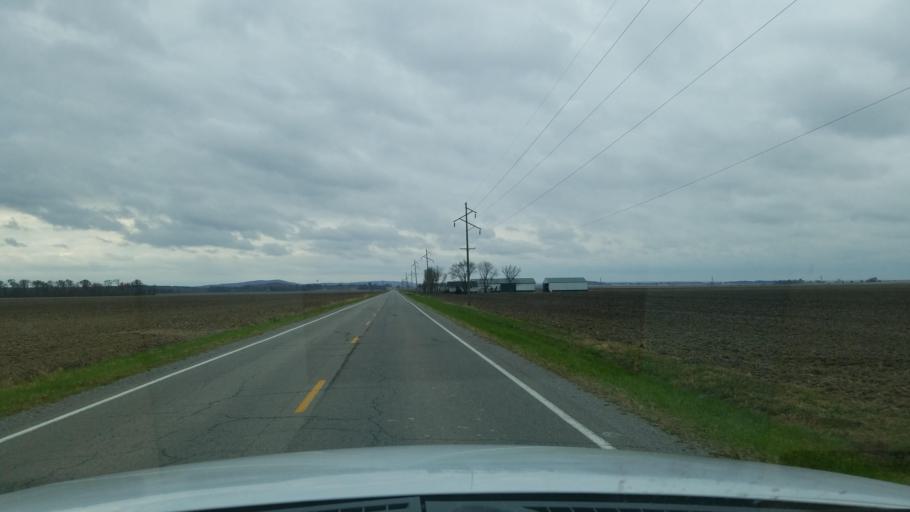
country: US
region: Illinois
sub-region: Saline County
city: Eldorado
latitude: 37.7864
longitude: -88.4382
